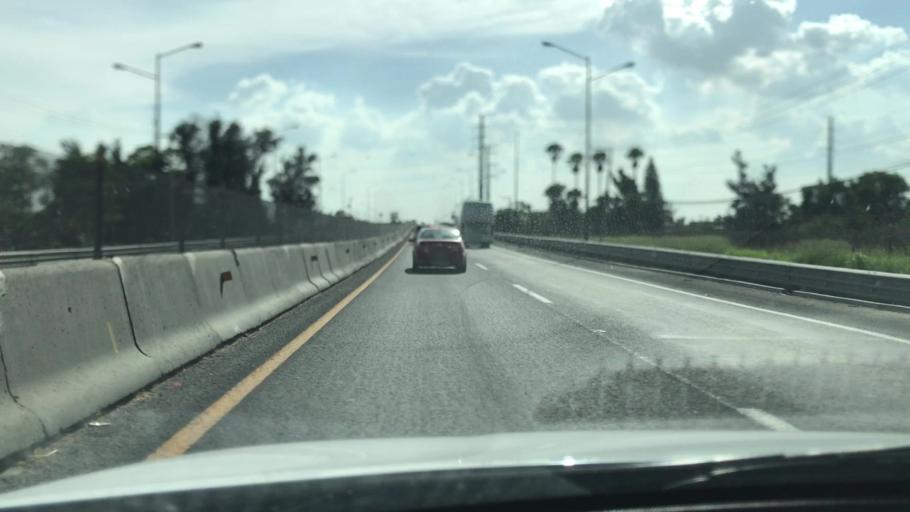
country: MX
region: Guanajuato
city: Villagran
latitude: 20.5088
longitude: -100.9872
